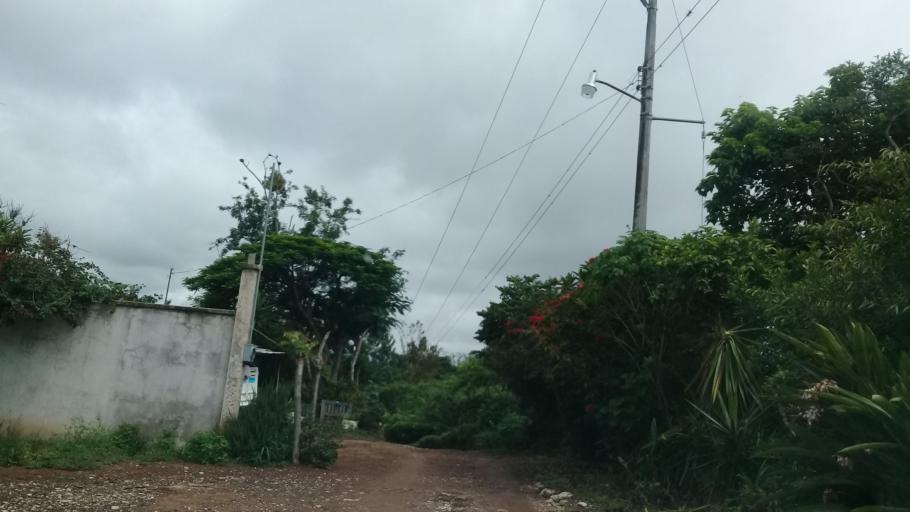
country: MX
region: Veracruz
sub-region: Emiliano Zapata
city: Jacarandas
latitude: 19.4780
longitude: -96.8502
